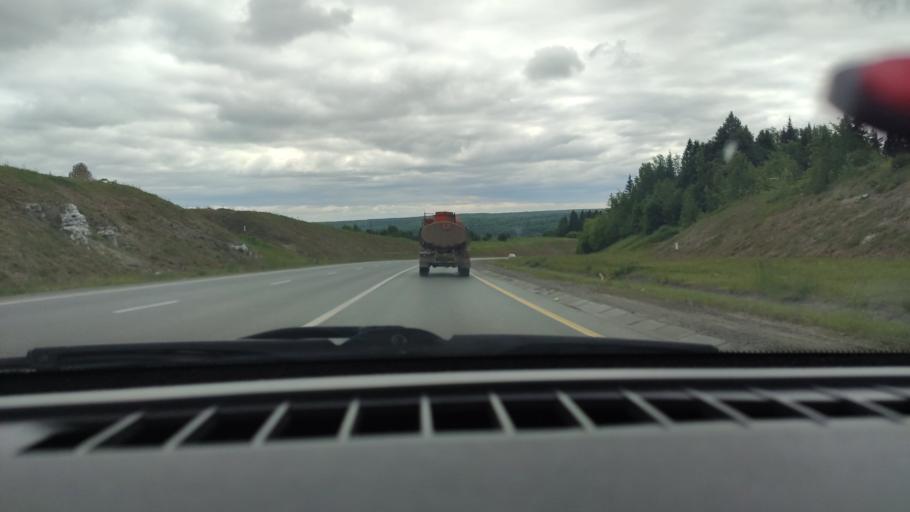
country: RU
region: Perm
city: Polazna
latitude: 58.2884
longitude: 56.4771
